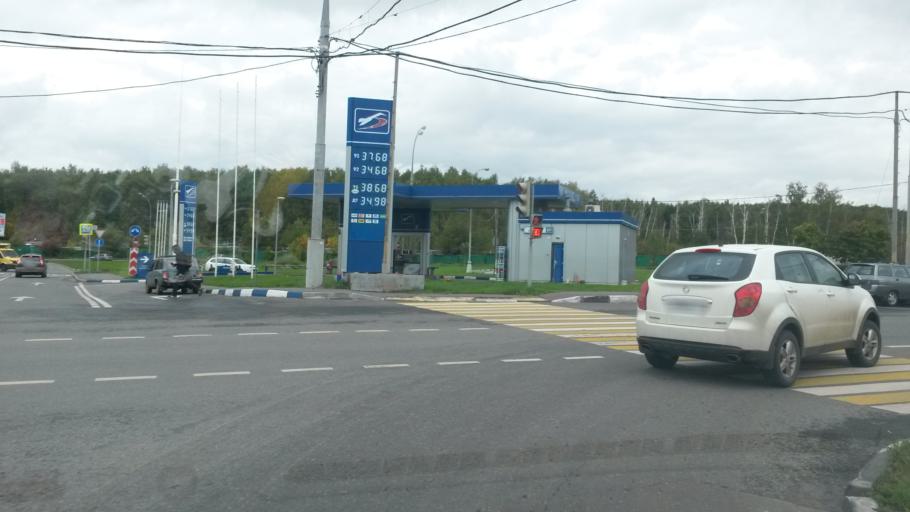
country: RU
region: Moskovskaya
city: Shcherbinka
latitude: 55.5499
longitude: 37.5433
